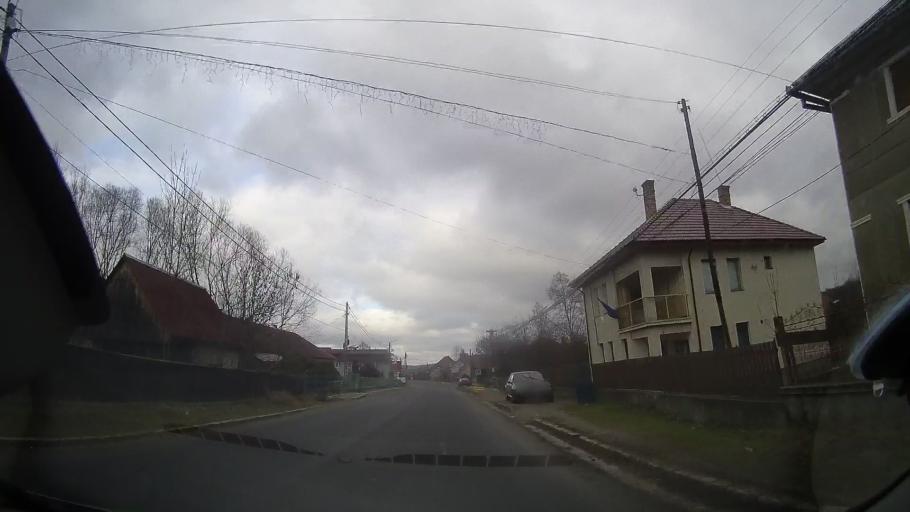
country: RO
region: Cluj
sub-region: Comuna Calatele
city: Calatele
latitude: 46.7642
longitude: 23.0081
